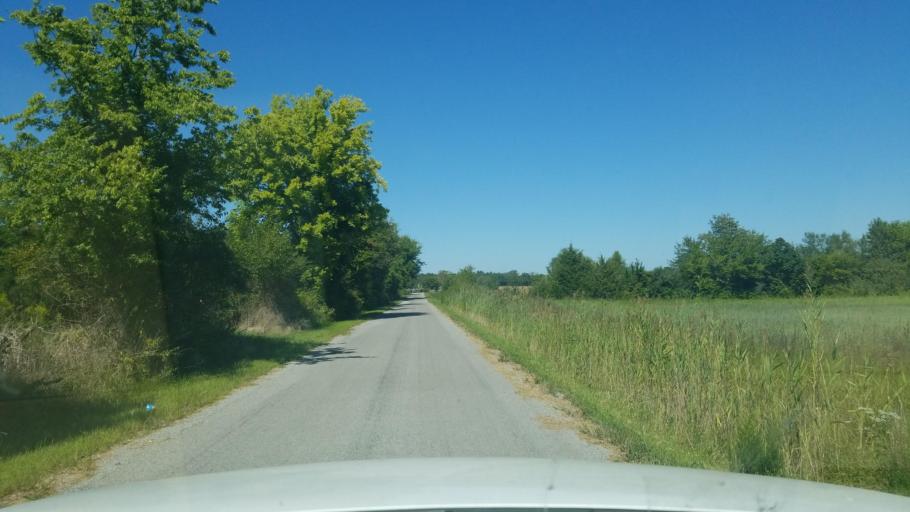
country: US
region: Illinois
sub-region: Saline County
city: Eldorado
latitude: 37.8587
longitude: -88.5119
